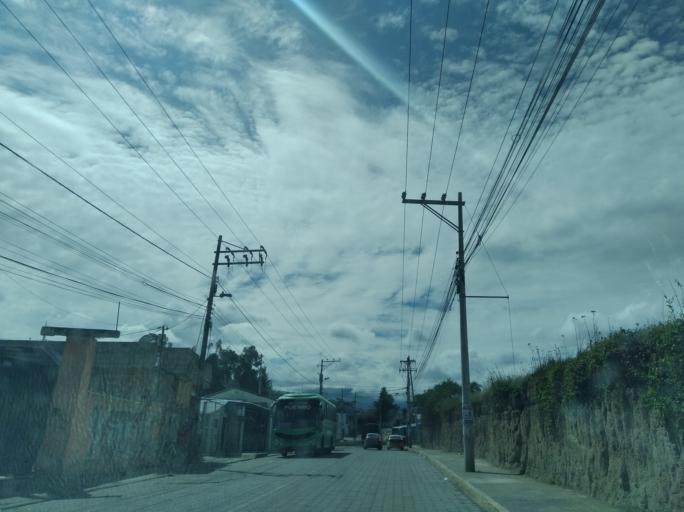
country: EC
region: Pichincha
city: Sangolqui
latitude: -0.2197
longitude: -78.3389
